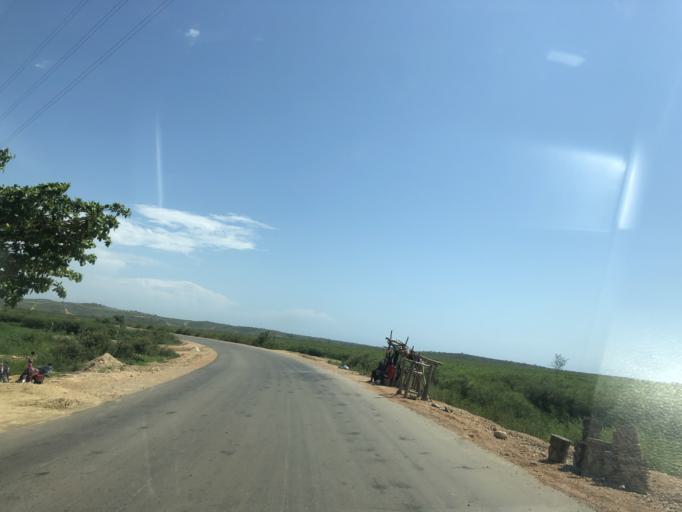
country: AO
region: Cuanza Sul
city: Sumbe
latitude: -10.8775
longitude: 13.8395
